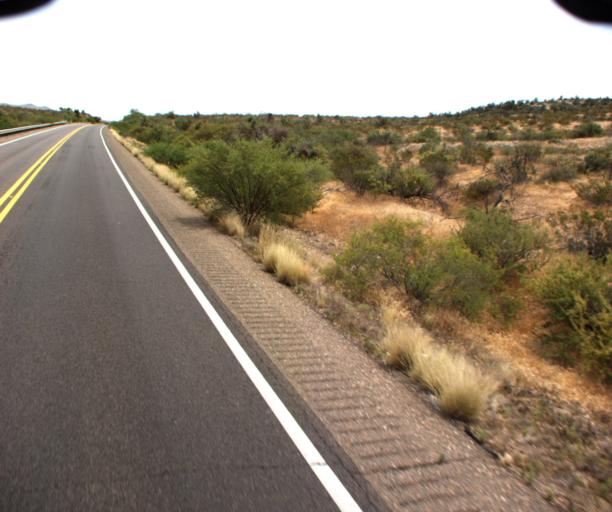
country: US
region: Arizona
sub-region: Gila County
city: Peridot
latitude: 33.2856
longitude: -110.3532
